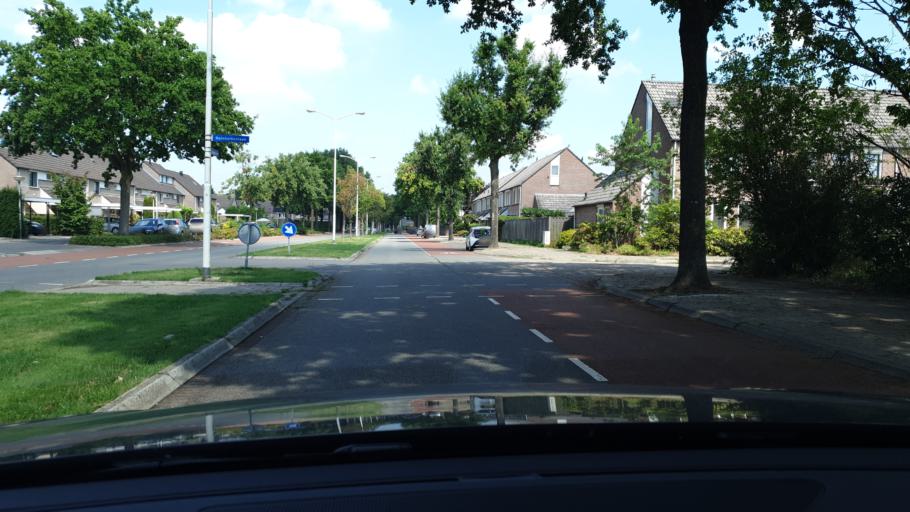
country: NL
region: North Brabant
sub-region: Gemeente Son en Breugel
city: Son
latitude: 51.4876
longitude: 5.4491
